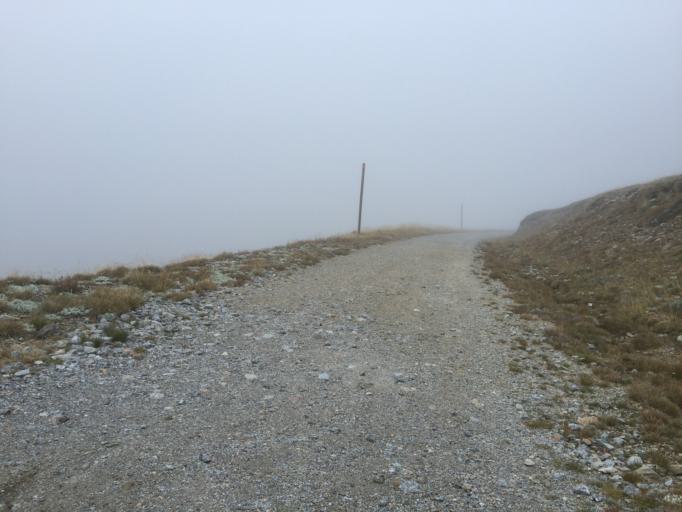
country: AU
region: New South Wales
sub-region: Snowy River
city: Jindabyne
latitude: -36.4511
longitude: 148.2755
